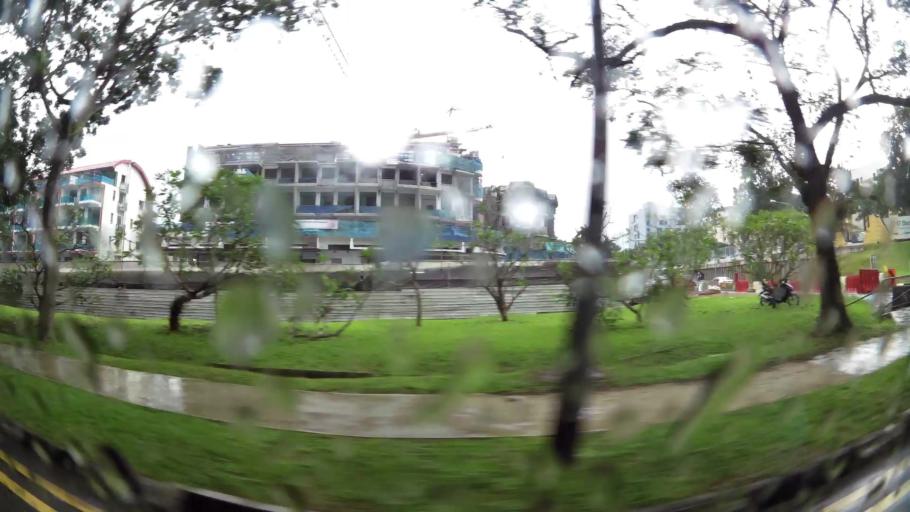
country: MY
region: Johor
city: Kampung Pasir Gudang Baru
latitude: 1.3923
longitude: 103.8504
